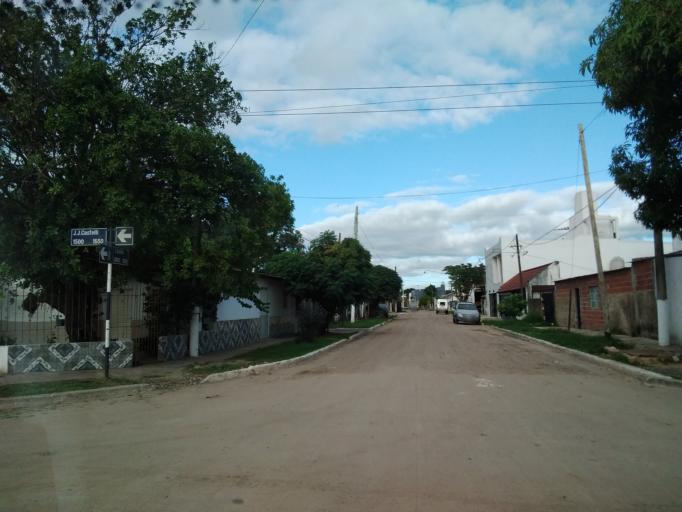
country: AR
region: Corrientes
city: Corrientes
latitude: -27.4778
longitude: -58.8095
